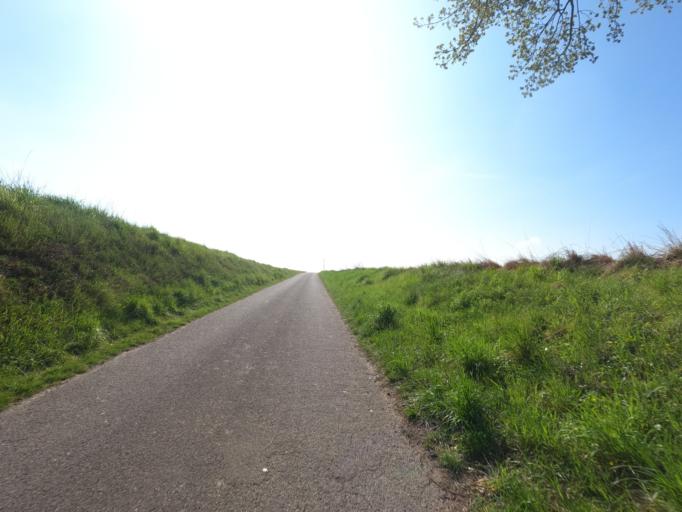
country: DE
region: North Rhine-Westphalia
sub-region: Regierungsbezirk Koln
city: Heinsberg
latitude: 51.0424
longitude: 6.0736
